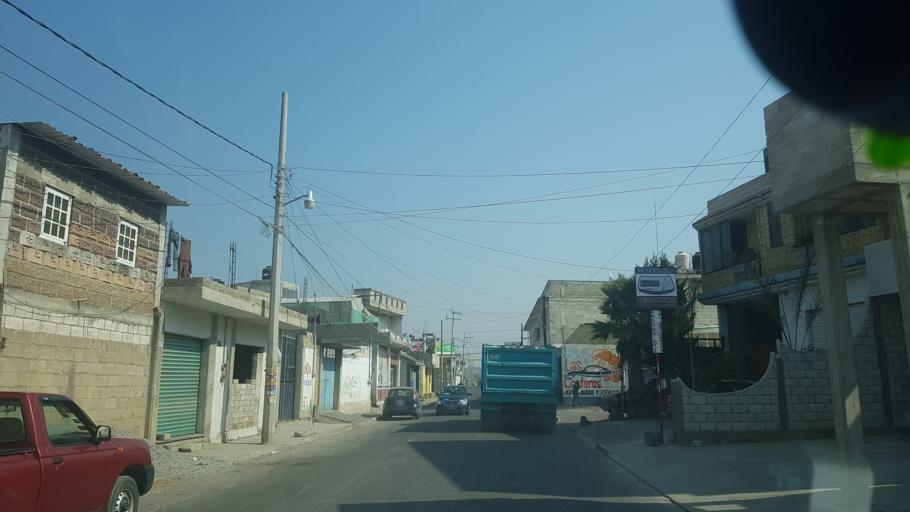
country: MX
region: Puebla
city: Nealtican
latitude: 19.0534
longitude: -98.4213
